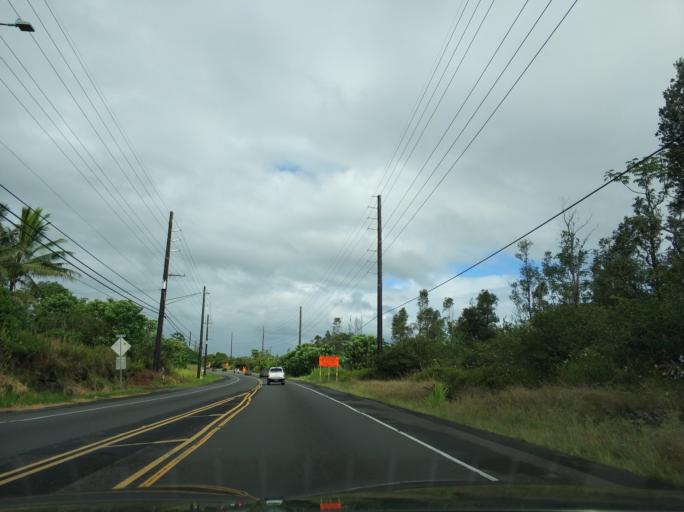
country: US
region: Hawaii
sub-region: Hawaii County
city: Orchidlands Estates
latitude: 19.5768
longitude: -155.0039
